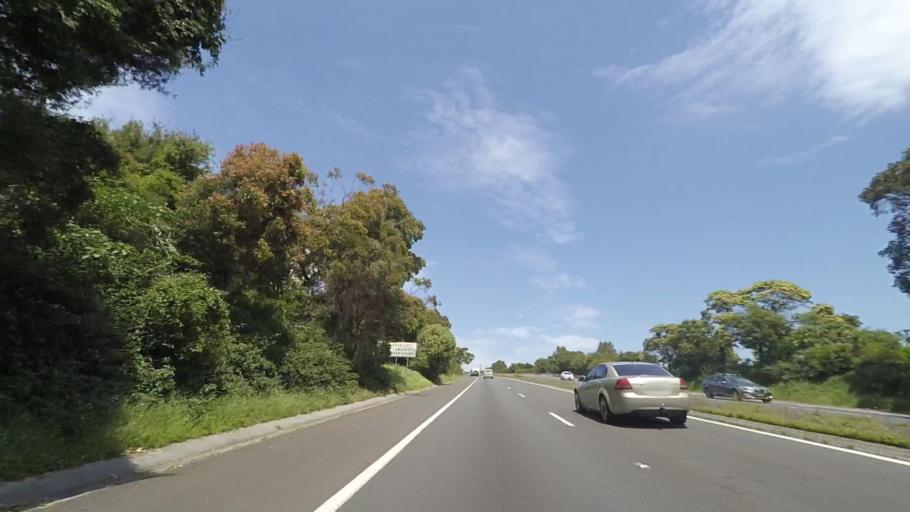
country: AU
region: New South Wales
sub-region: Kiama
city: Kiama
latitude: -34.6708
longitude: 150.8436
